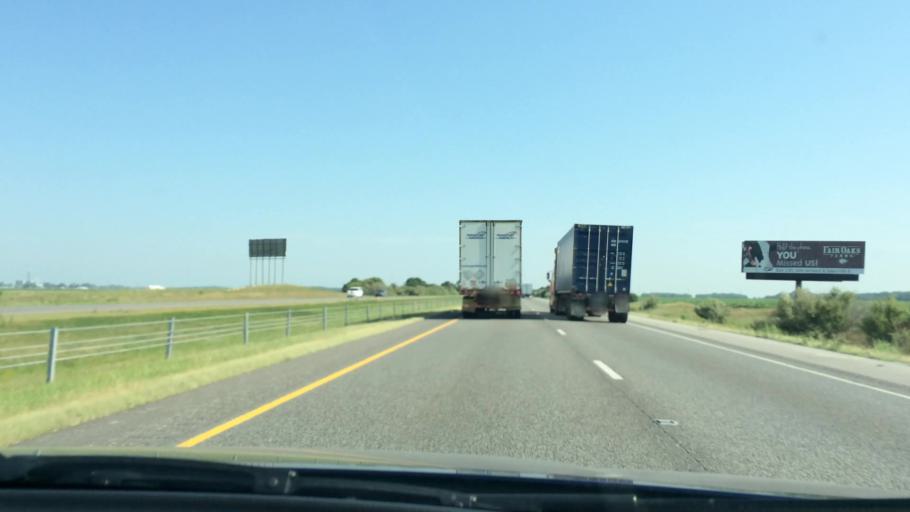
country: US
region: Indiana
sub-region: Newton County
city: Roselawn
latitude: 41.0591
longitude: -87.2704
